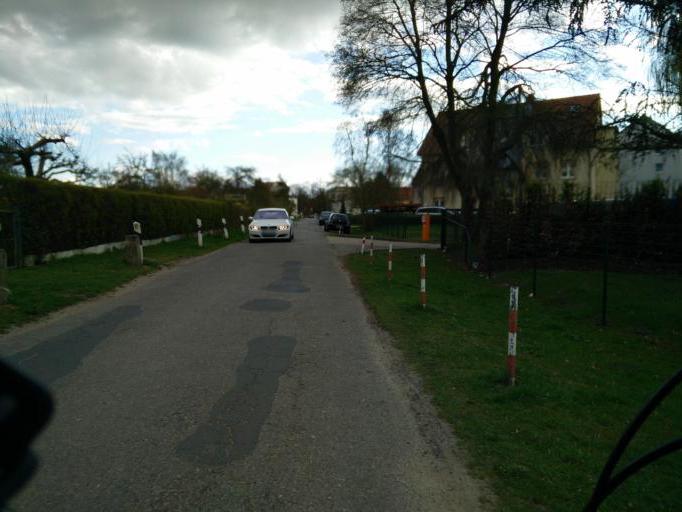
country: DE
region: Mecklenburg-Vorpommern
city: Rostock
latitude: 54.1056
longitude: 12.1170
